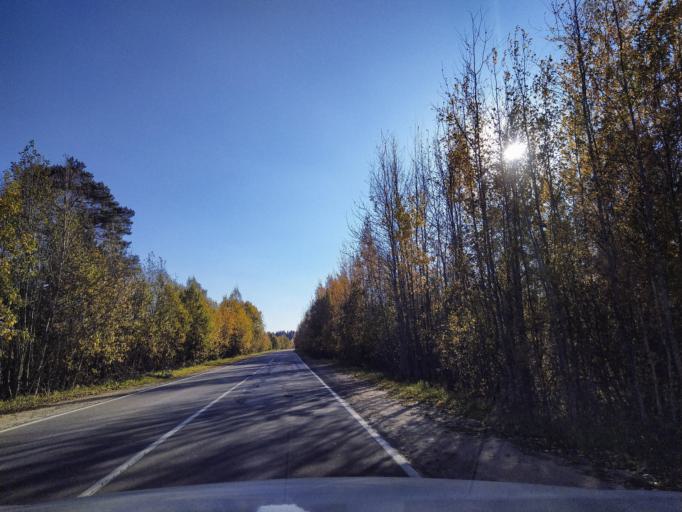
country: RU
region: Leningrad
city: Siverskiy
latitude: 59.3154
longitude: 30.0336
